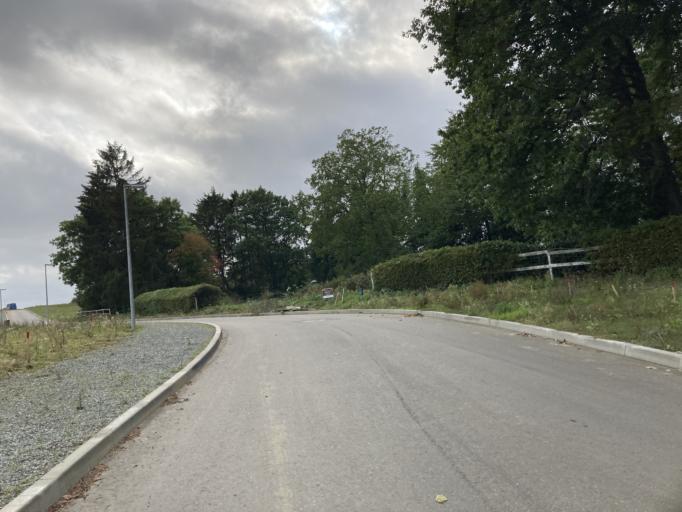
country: DK
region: South Denmark
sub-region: Kolding Kommune
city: Sonder Bjert
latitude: 55.4525
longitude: 9.5627
